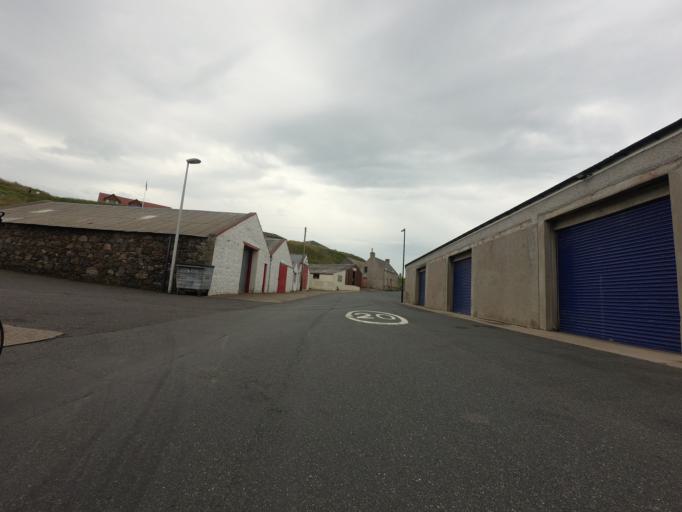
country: GB
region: Scotland
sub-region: Aberdeenshire
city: Whitehills
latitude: 57.6799
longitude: -2.5779
